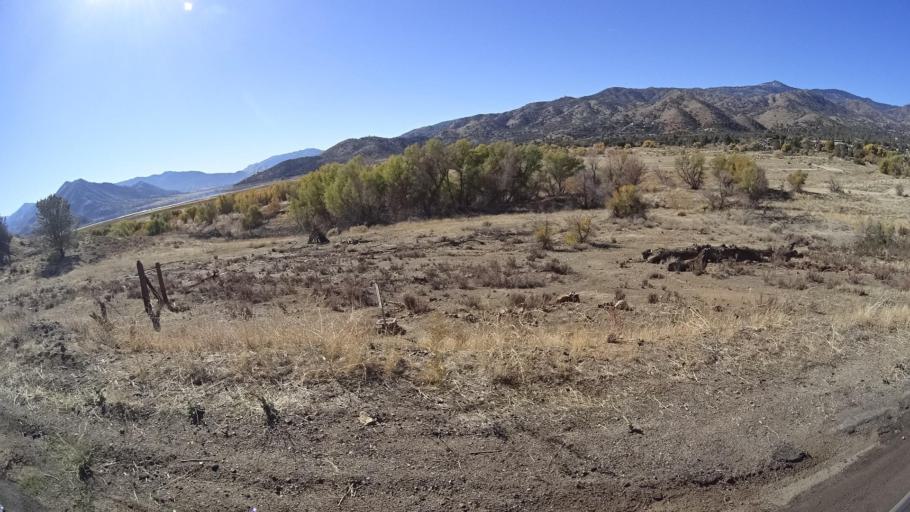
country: US
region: California
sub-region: Kern County
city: Wofford Heights
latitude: 35.7041
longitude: -118.4464
